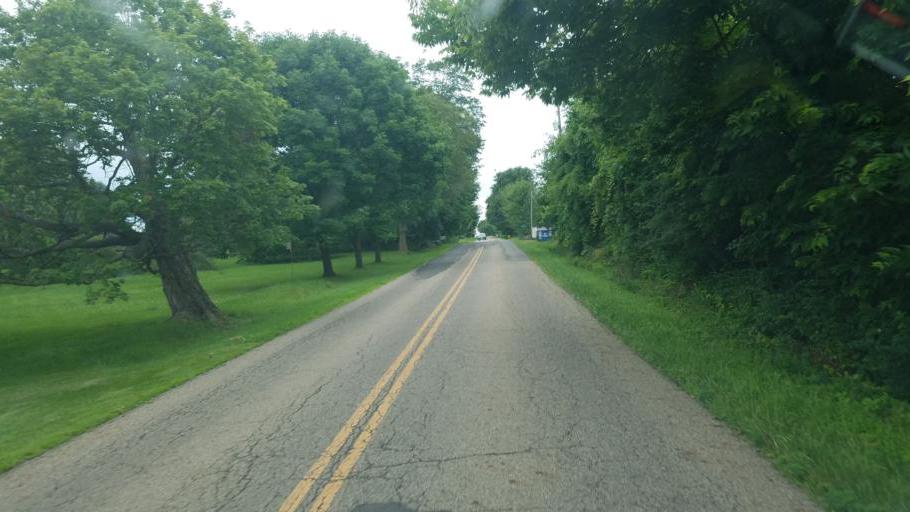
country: US
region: Ohio
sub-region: Knox County
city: Centerburg
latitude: 40.2737
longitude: -82.6701
